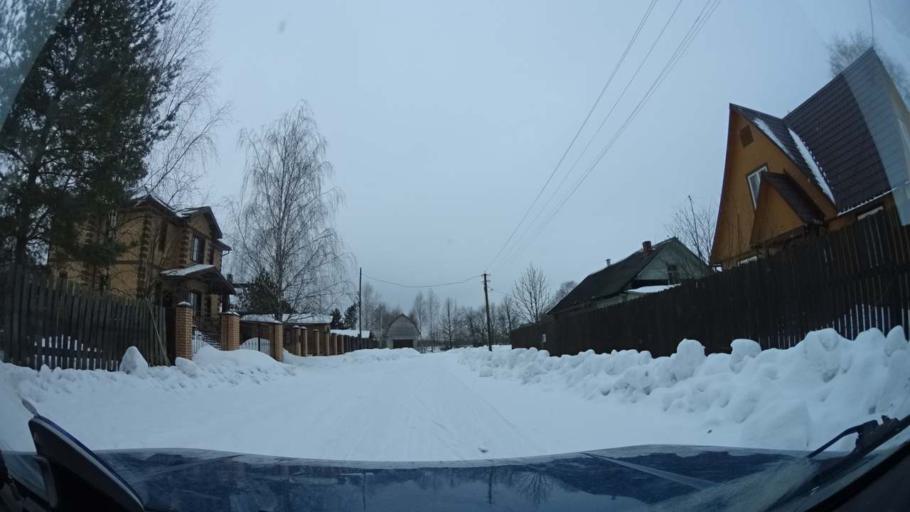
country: RU
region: Tverskaya
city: Radchenko
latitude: 56.7016
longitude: 36.3852
